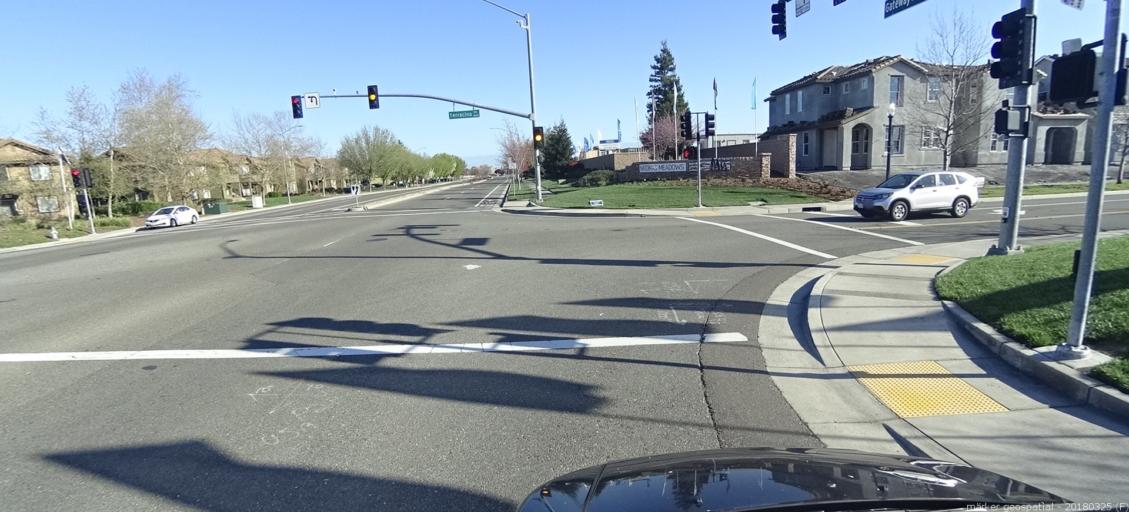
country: US
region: California
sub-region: Sacramento County
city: Rio Linda
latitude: 38.6522
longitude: -121.5026
